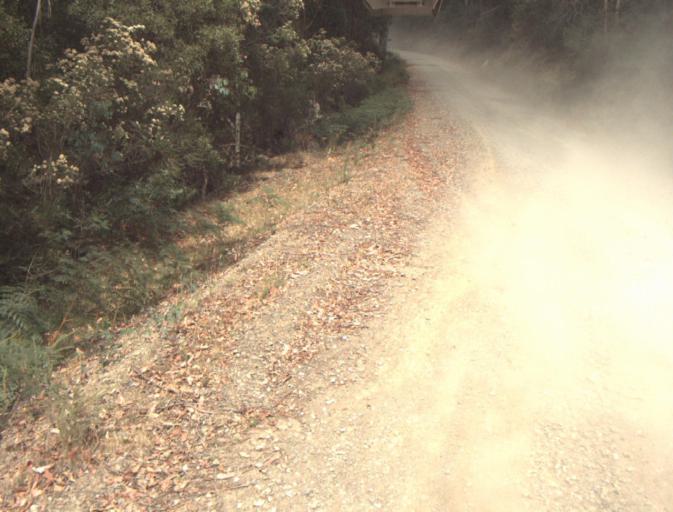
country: AU
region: Tasmania
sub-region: Dorset
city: Scottsdale
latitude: -41.4183
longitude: 147.5217
